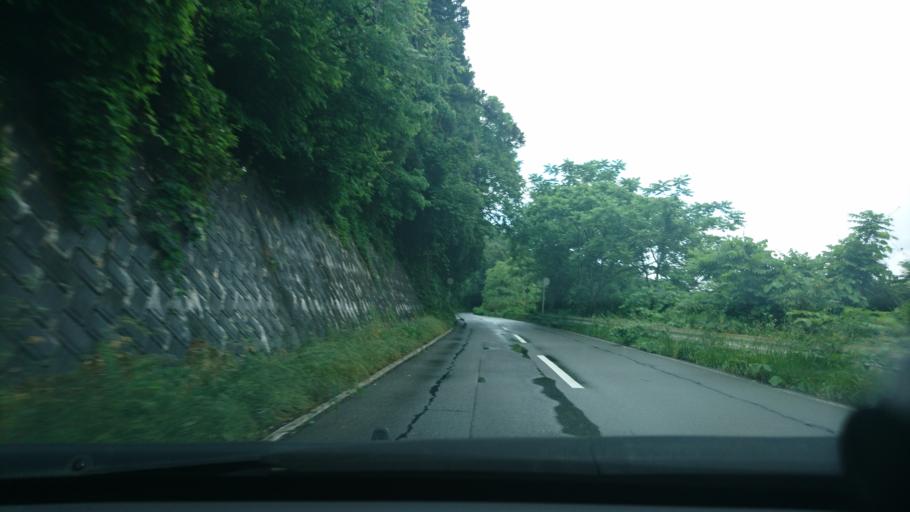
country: JP
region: Miyagi
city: Wakuya
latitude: 38.6686
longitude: 141.2833
